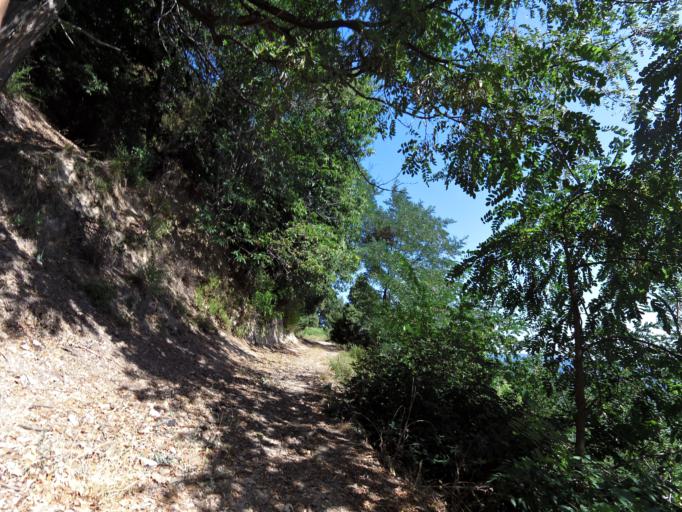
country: IT
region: Calabria
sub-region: Provincia di Reggio Calabria
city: Bivongi
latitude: 38.5060
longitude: 16.4371
